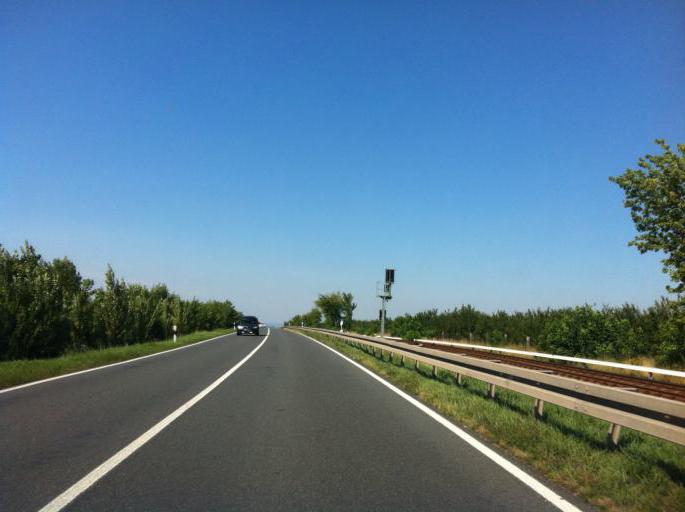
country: DE
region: Thuringia
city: Dollstadt
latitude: 51.0855
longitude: 10.7963
